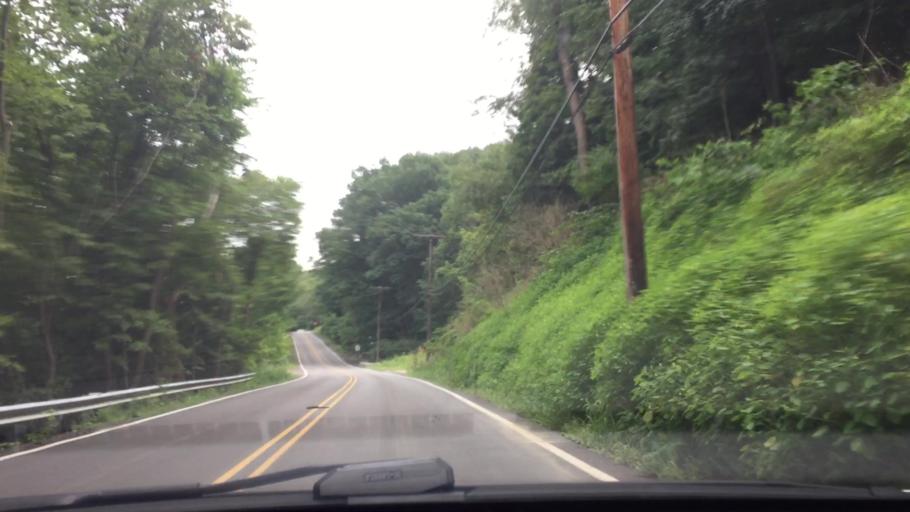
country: US
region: Pennsylvania
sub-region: Allegheny County
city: Rennerdale
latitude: 40.3807
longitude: -80.1542
